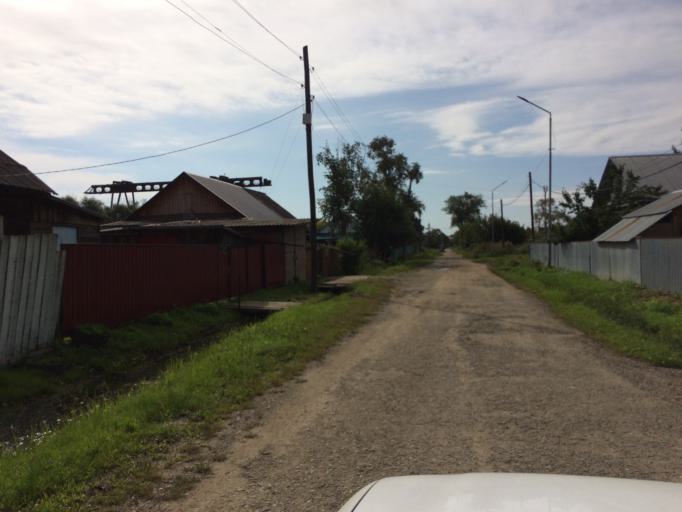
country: RU
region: Primorskiy
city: Dal'nerechensk
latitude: 45.9344
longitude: 133.7469
